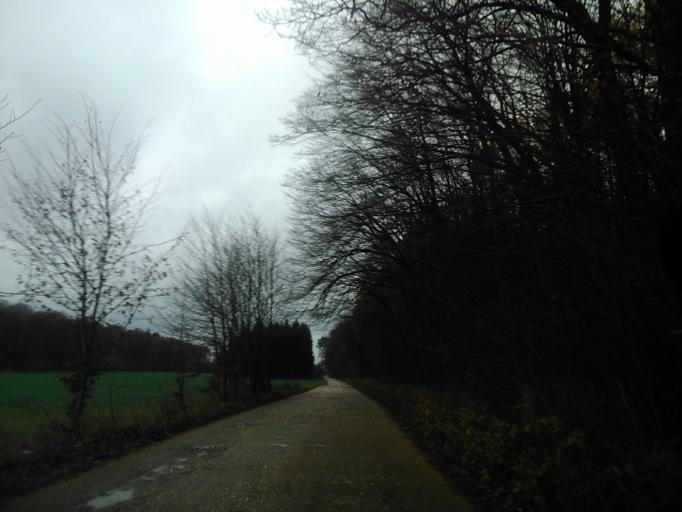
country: PL
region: Kujawsko-Pomorskie
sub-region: Powiat golubsko-dobrzynski
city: Radomin
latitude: 53.1295
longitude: 19.1679
